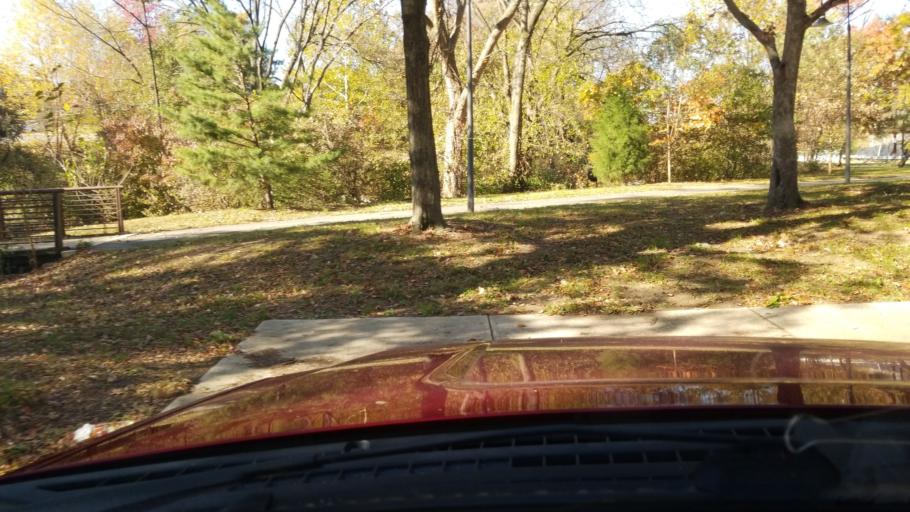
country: US
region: Maryland
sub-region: Prince George's County
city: Fairmount Heights
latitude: 38.9002
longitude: -76.9408
